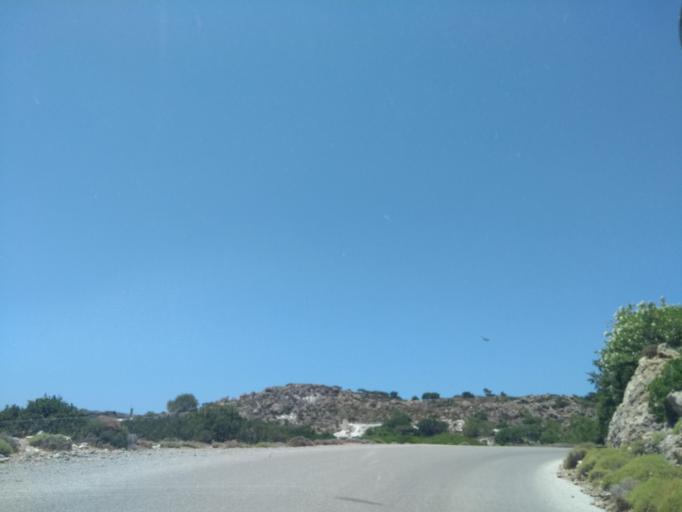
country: GR
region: Crete
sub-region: Nomos Chanias
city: Vryses
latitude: 35.3303
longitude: 23.5443
